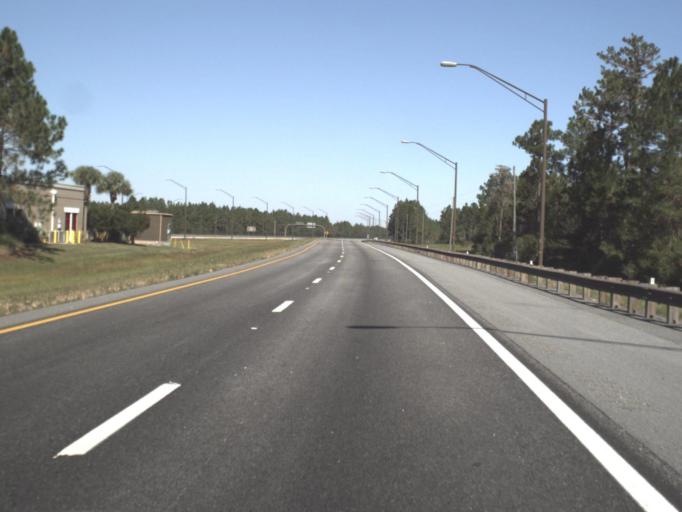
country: US
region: Florida
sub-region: Pasco County
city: Odessa
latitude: 28.2554
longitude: -82.5492
